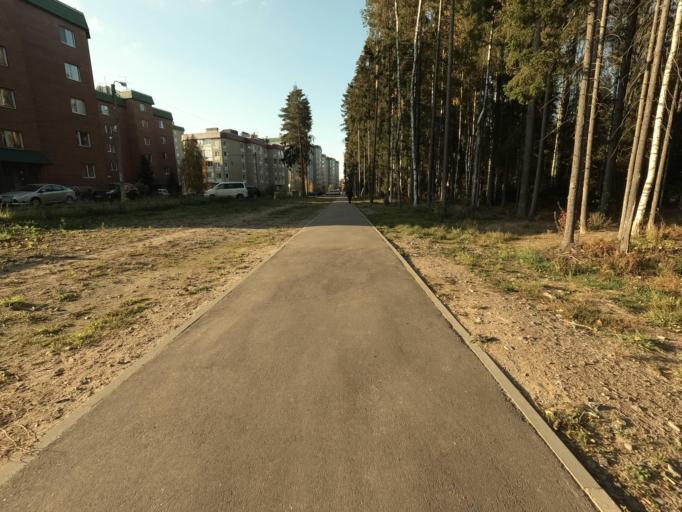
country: RU
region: Leningrad
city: Sertolovo
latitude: 60.1452
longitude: 30.2282
